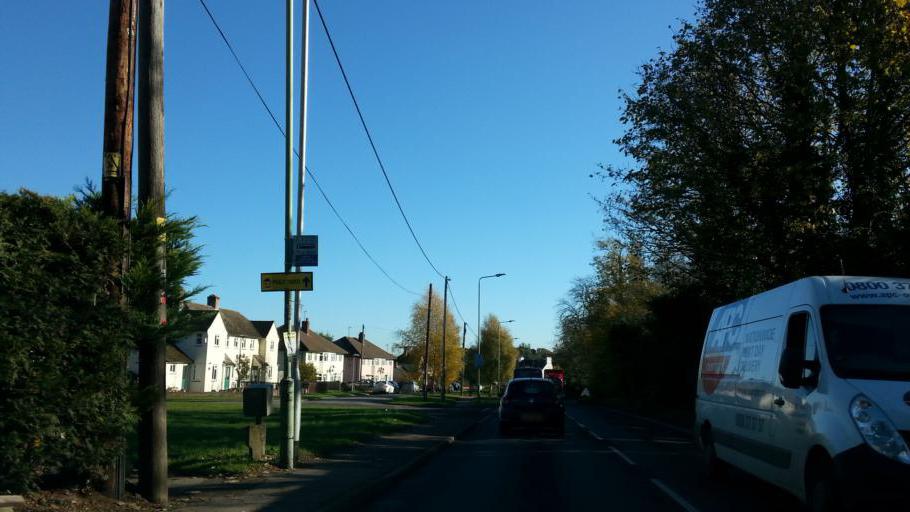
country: GB
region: England
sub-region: Suffolk
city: Woodbridge
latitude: 52.1055
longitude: 1.3259
